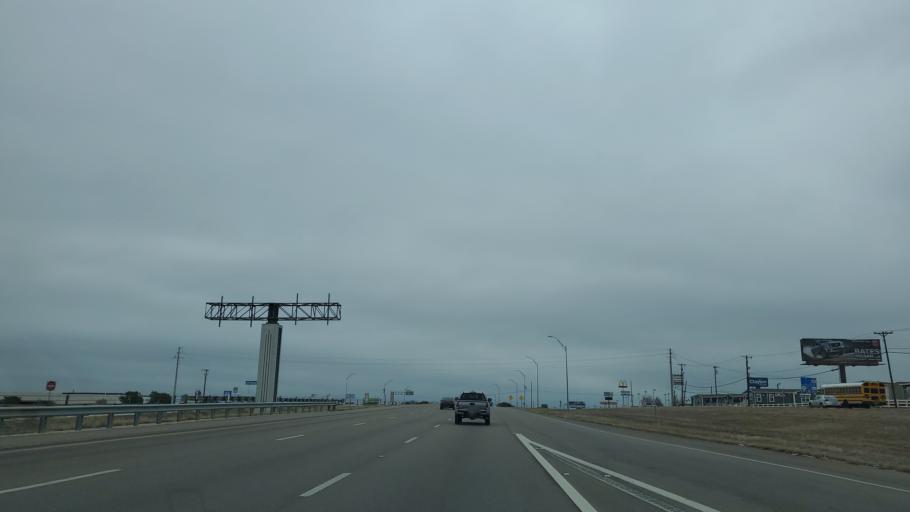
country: US
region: Texas
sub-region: Bell County
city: Killeen
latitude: 31.0824
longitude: -97.7029
